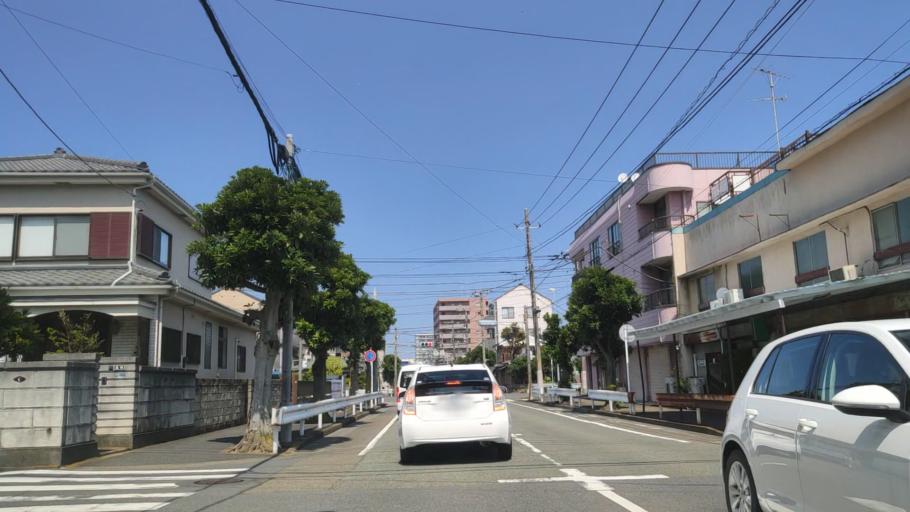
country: JP
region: Kanagawa
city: Hiratsuka
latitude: 35.3304
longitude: 139.3564
